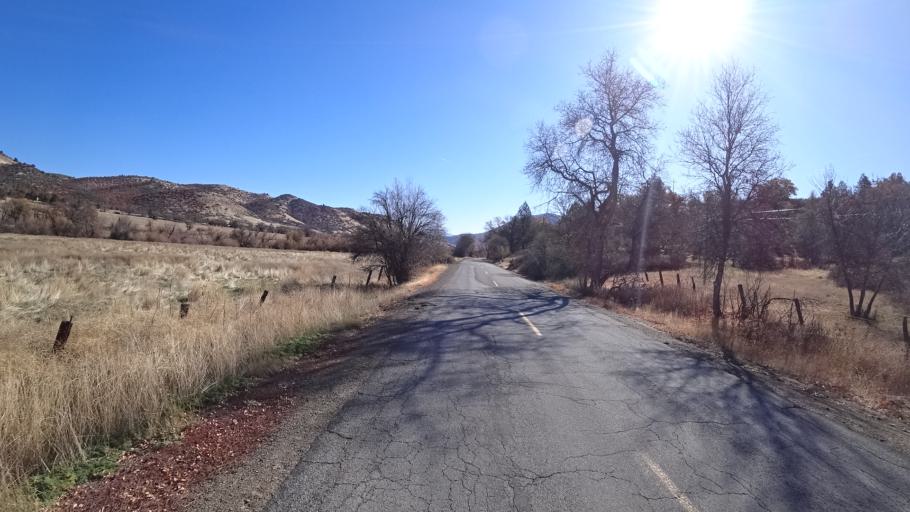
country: US
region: California
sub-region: Siskiyou County
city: Montague
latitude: 41.9178
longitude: -122.5659
